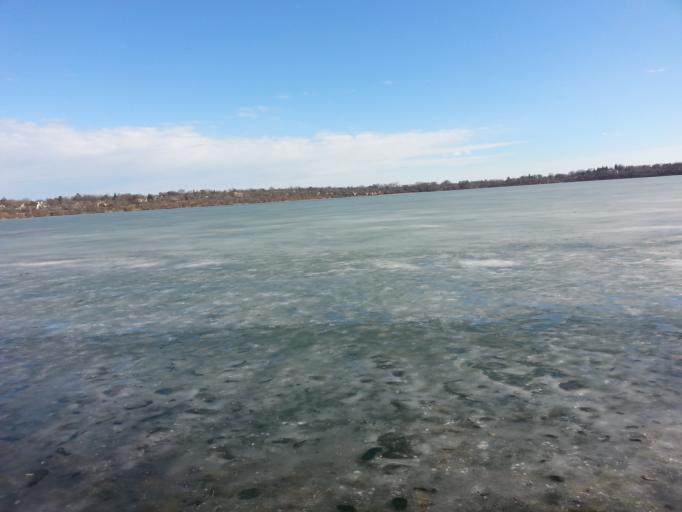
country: US
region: Minnesota
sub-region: Hennepin County
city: Saint Louis Park
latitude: 44.9279
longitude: -93.3079
